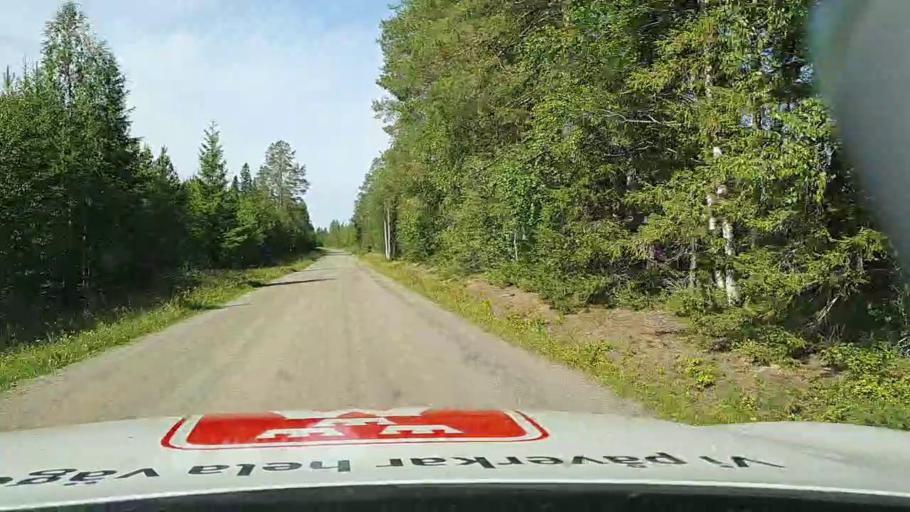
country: SE
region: Jaemtland
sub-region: Stroemsunds Kommun
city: Stroemsund
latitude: 63.7223
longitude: 15.2682
